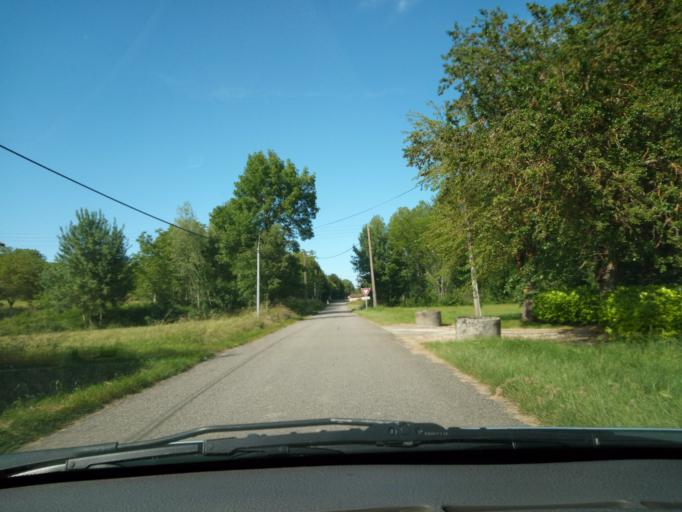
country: FR
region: Midi-Pyrenees
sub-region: Departement du Lot
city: Castelnau-Montratier
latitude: 44.2383
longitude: 1.3388
